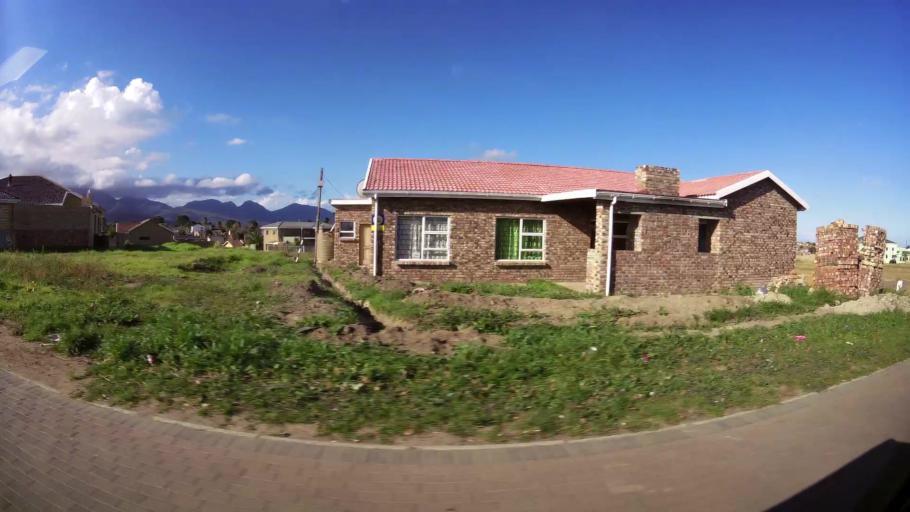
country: ZA
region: Western Cape
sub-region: Eden District Municipality
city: George
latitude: -33.9703
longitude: 22.4825
